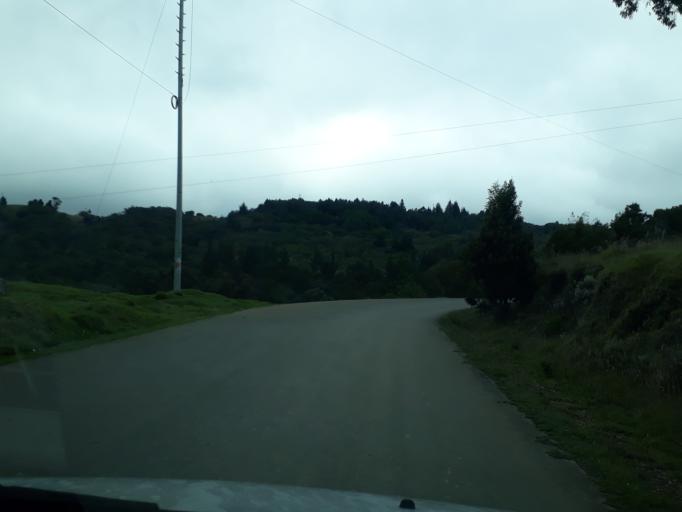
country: CO
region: Cundinamarca
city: Cucunuba
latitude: 5.1978
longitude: -73.7891
